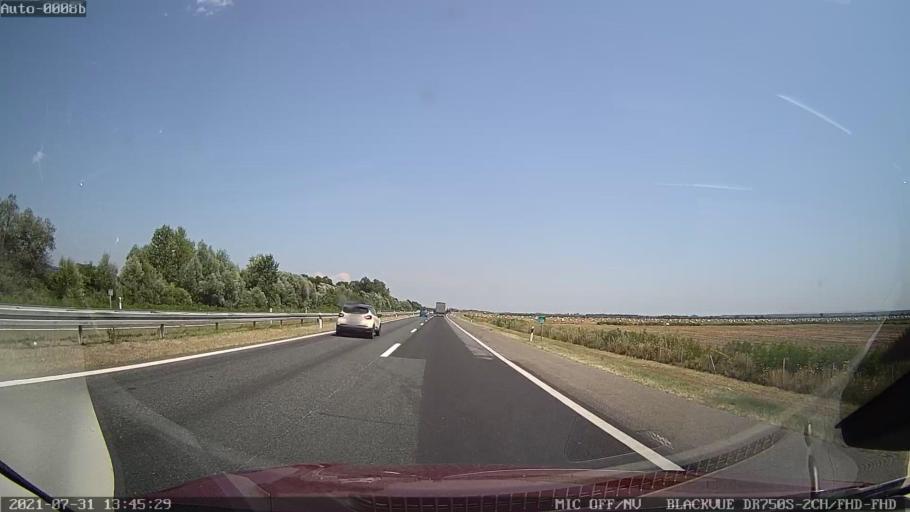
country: HR
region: Brodsko-Posavska
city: Sibinj
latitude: 45.1674
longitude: 17.8757
